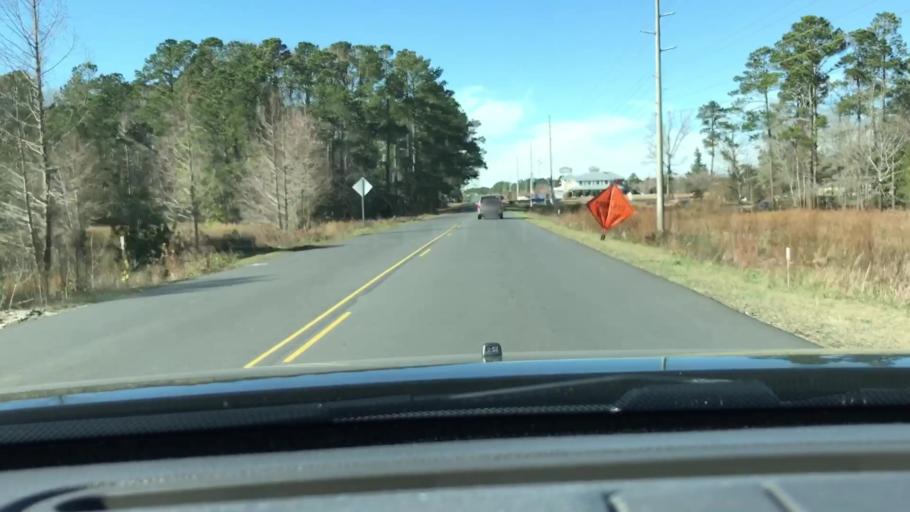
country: US
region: North Carolina
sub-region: Brunswick County
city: Shallotte
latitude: 33.9707
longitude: -78.3960
